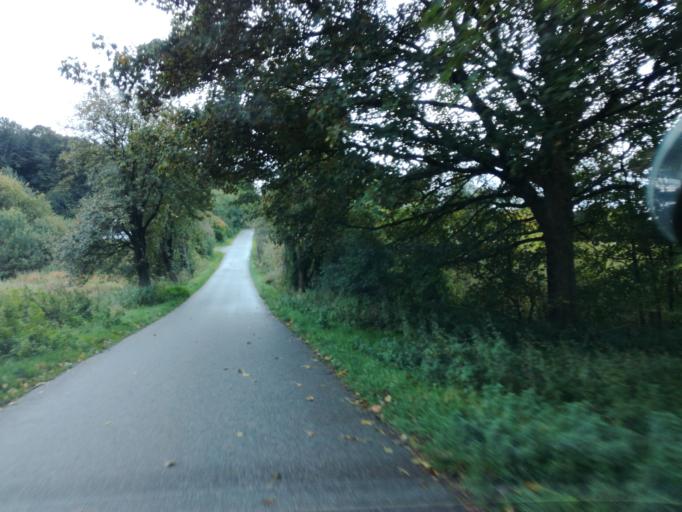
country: DK
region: South Denmark
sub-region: Fredericia Kommune
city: Fredericia
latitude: 55.6034
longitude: 9.7171
